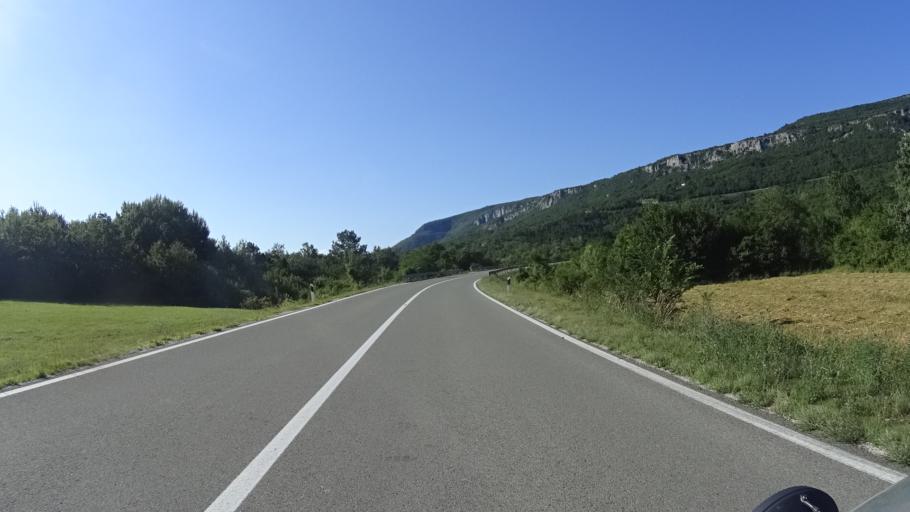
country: HR
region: Istarska
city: Lovran
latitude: 45.3225
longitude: 14.1373
